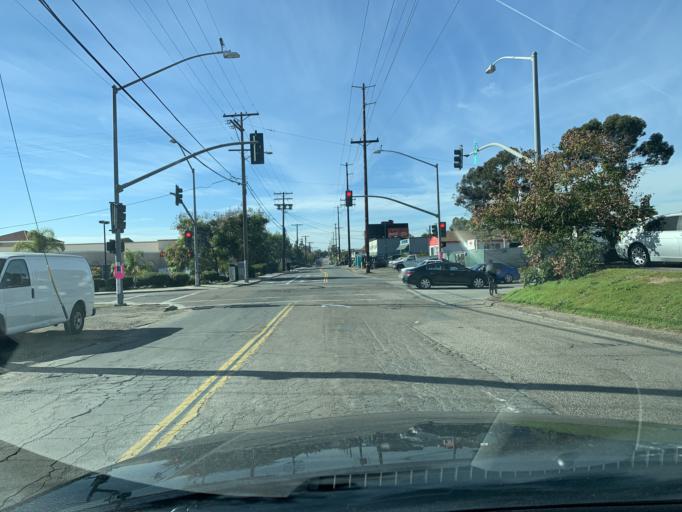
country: US
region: California
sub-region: San Diego County
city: Lemon Grove
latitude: 32.7446
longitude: -117.0339
